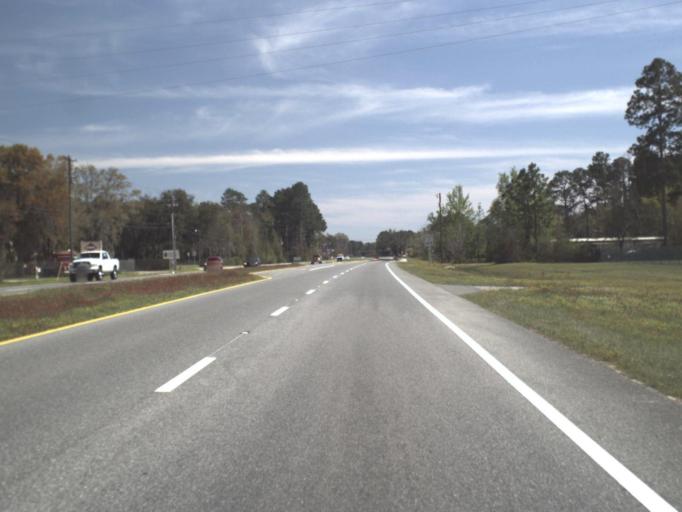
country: US
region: Florida
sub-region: Bay County
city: Lynn Haven
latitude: 30.2965
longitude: -85.6450
